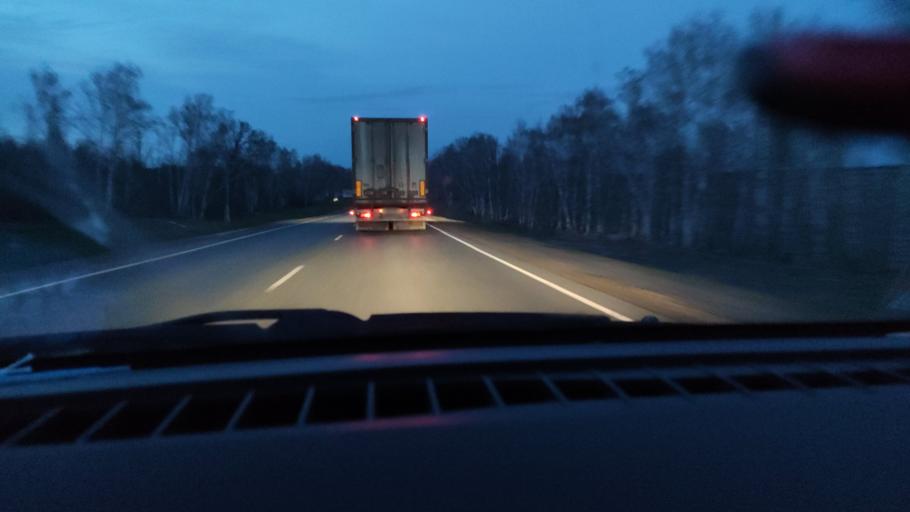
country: RU
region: Saratov
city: Sennoy
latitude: 52.1244
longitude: 46.8512
